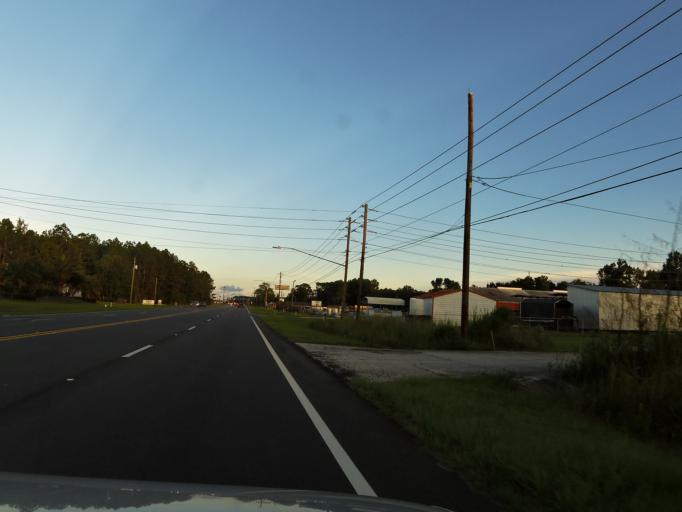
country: US
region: Georgia
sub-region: Camden County
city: Kingsland
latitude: 30.7962
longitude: -81.6723
